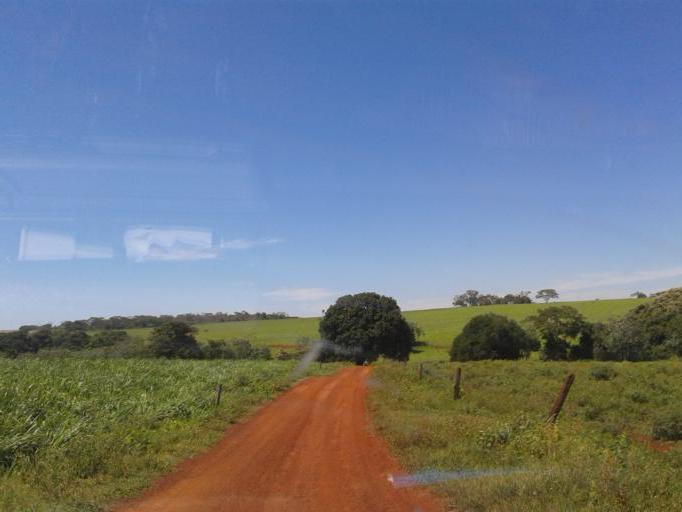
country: BR
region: Minas Gerais
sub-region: Capinopolis
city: Capinopolis
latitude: -18.6269
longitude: -49.6121
